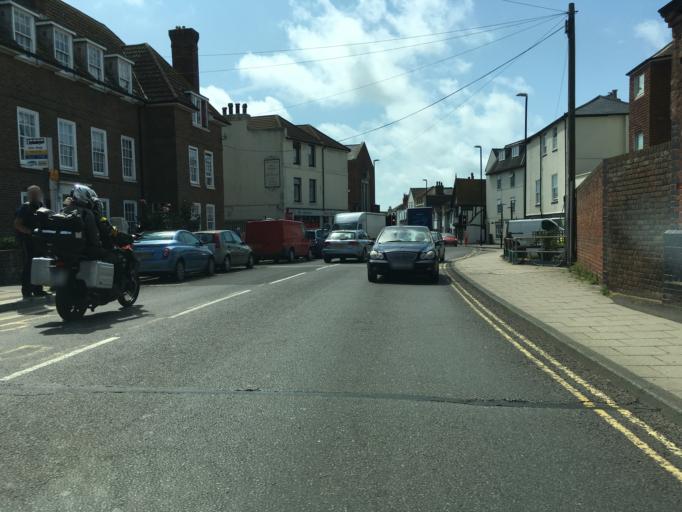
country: GB
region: England
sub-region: East Sussex
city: Hastings
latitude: 50.8576
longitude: 0.5930
